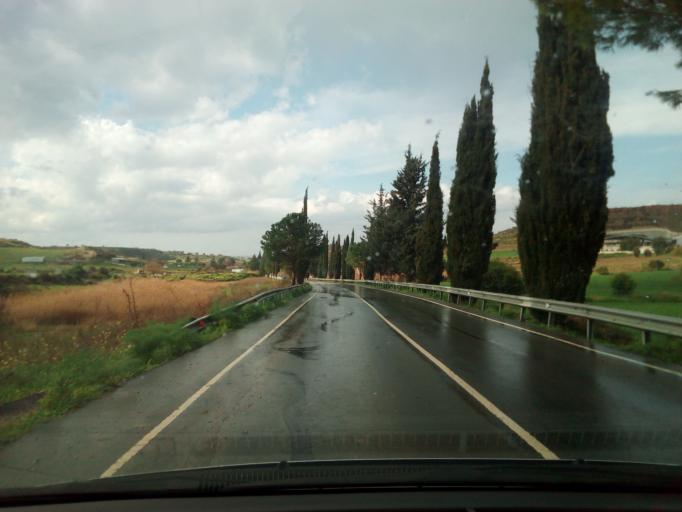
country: CY
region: Pafos
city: Polis
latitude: 35.0244
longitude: 32.4438
